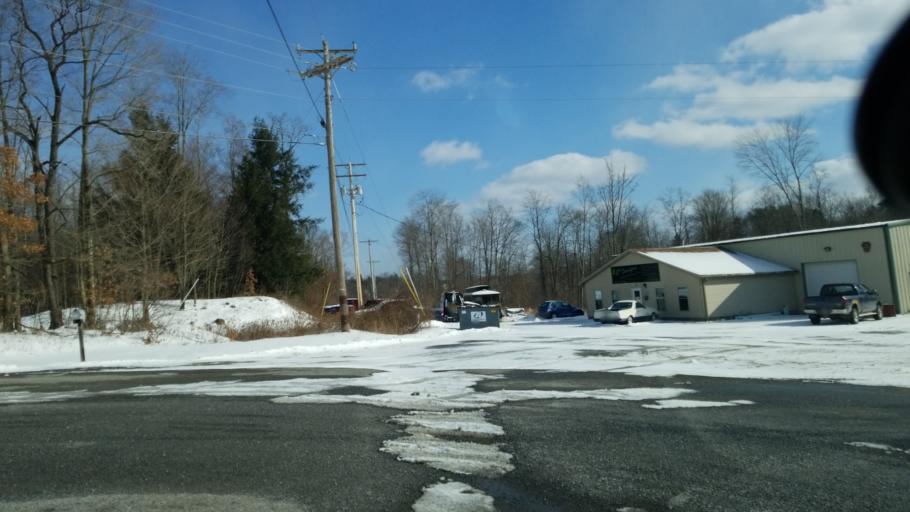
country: US
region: Pennsylvania
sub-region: Jefferson County
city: Falls Creek
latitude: 41.1460
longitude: -78.8128
